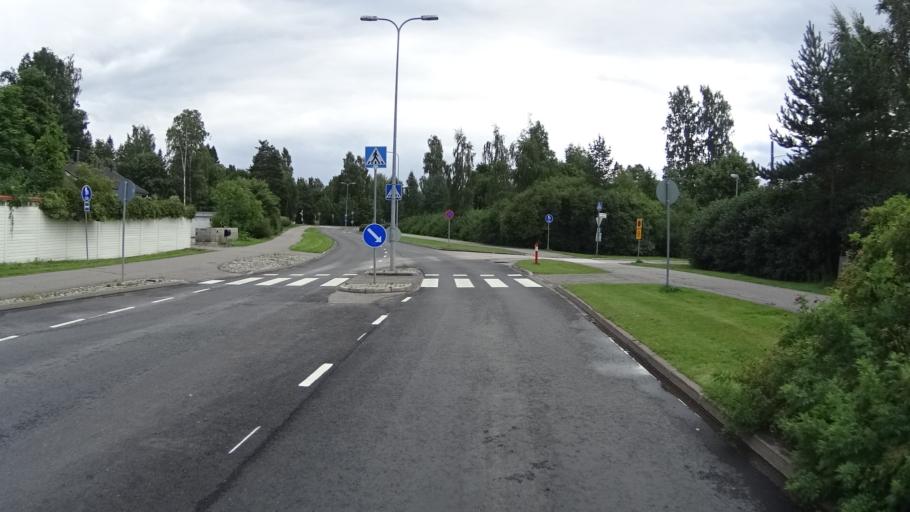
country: FI
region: Uusimaa
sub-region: Helsinki
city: Kauniainen
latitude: 60.2242
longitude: 24.7428
